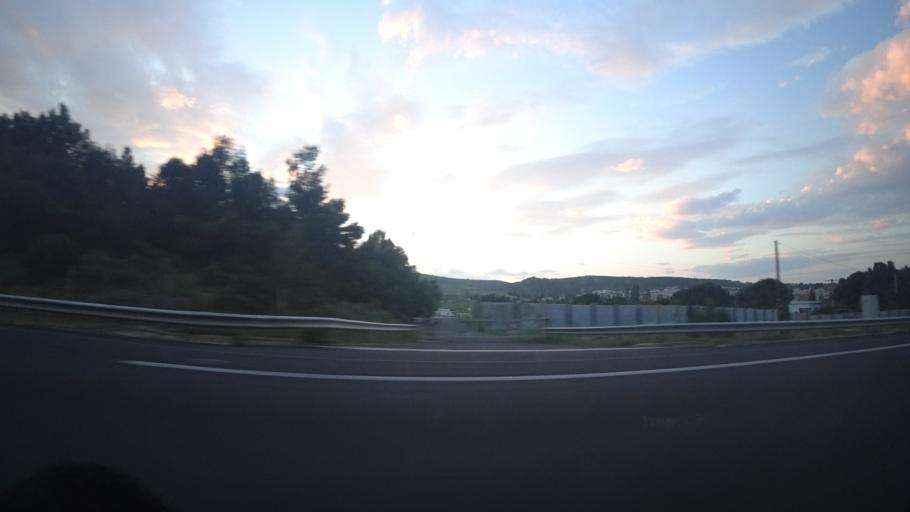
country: FR
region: Languedoc-Roussillon
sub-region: Departement de l'Aude
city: Peyriac-de-Mer
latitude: 43.1280
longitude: 2.9624
